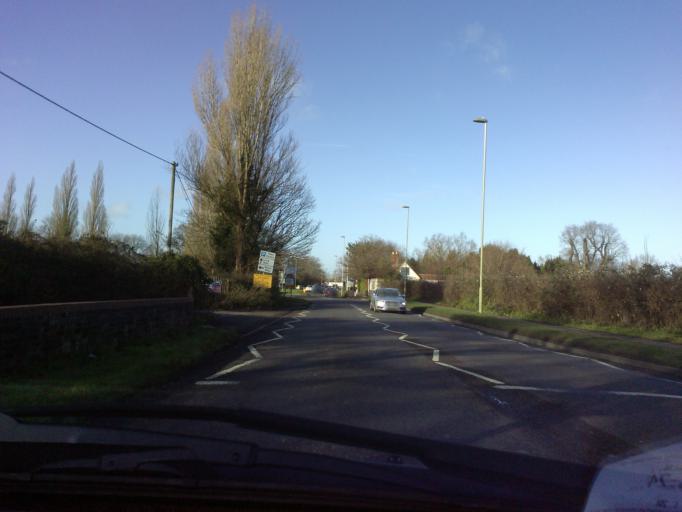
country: GB
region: England
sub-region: Hampshire
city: Romsey
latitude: 50.9871
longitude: -1.4883
